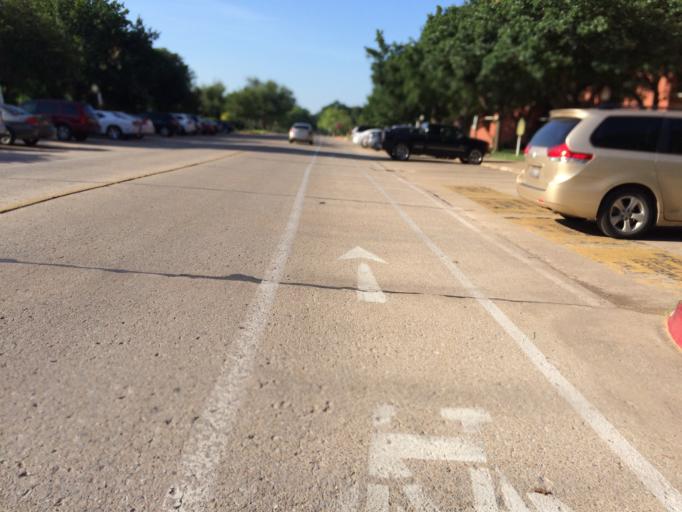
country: US
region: Oklahoma
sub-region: Cleveland County
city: Norman
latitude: 35.2008
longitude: -97.4444
